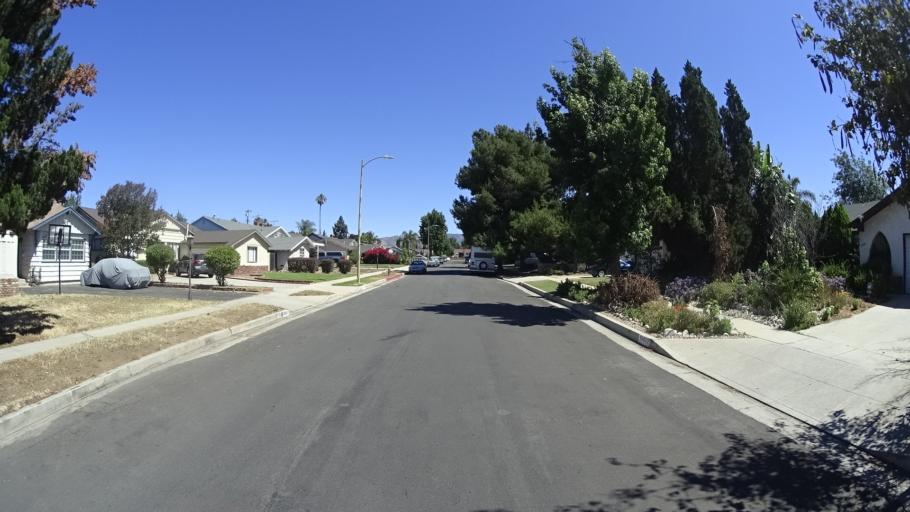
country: US
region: California
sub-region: Los Angeles County
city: San Fernando
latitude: 34.2518
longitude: -118.4598
